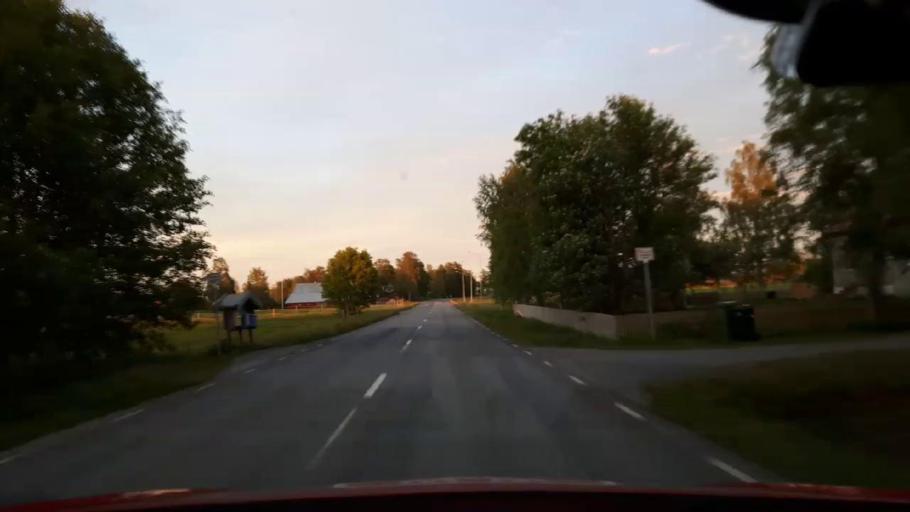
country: SE
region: Jaemtland
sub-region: OEstersunds Kommun
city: Ostersund
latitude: 63.1220
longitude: 14.7088
